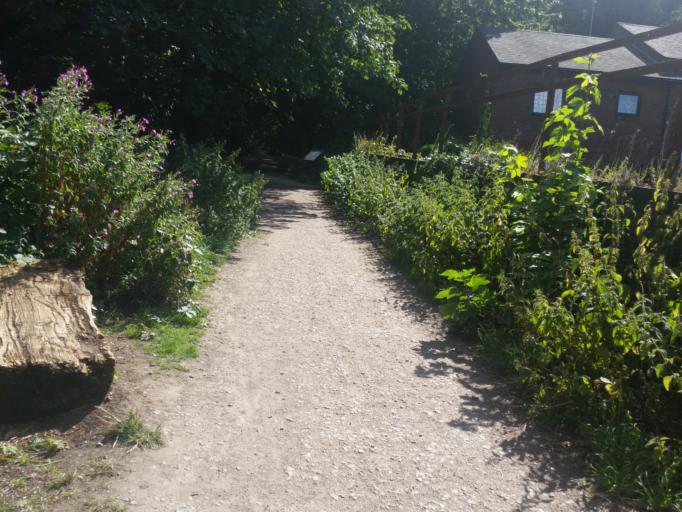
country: GB
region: England
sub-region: Greater London
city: Crouch End
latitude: 51.5882
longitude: -0.1423
